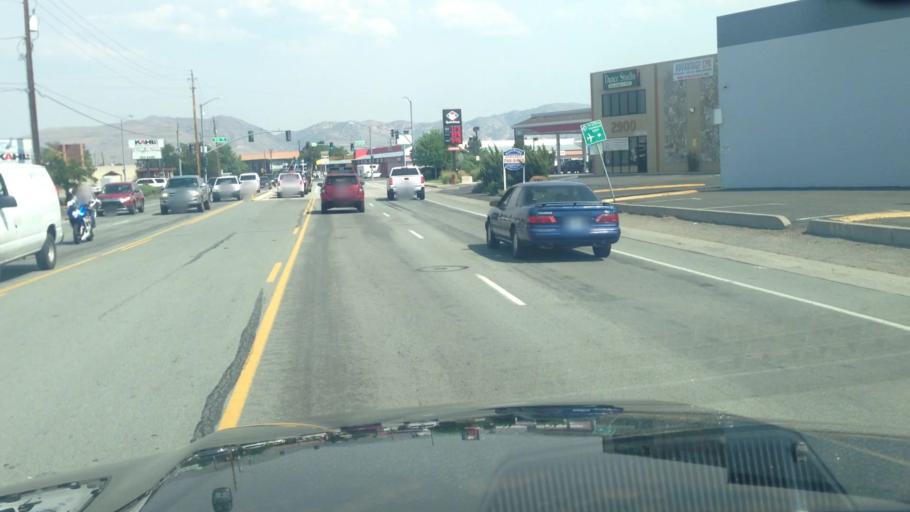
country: US
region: Nevada
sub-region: Washoe County
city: Sparks
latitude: 39.5181
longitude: -119.7789
